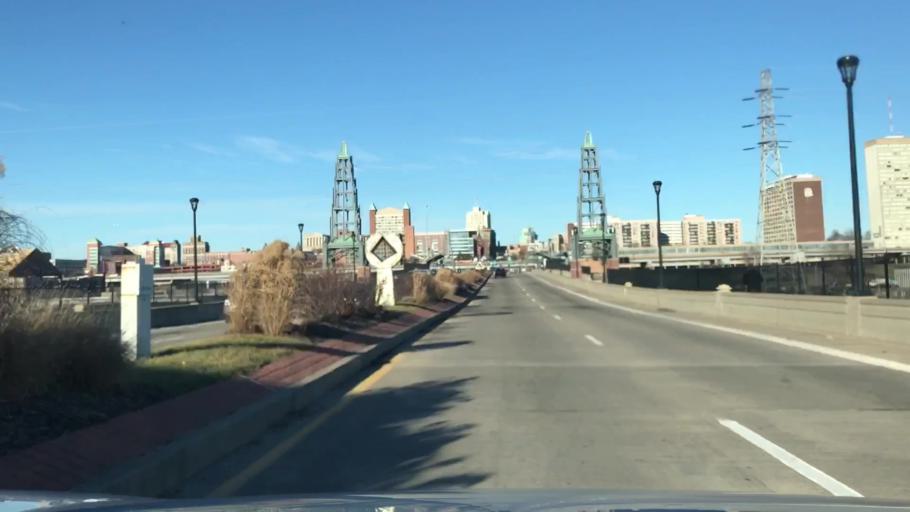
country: US
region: Missouri
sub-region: City of Saint Louis
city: St. Louis
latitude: 38.6277
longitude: -90.2361
